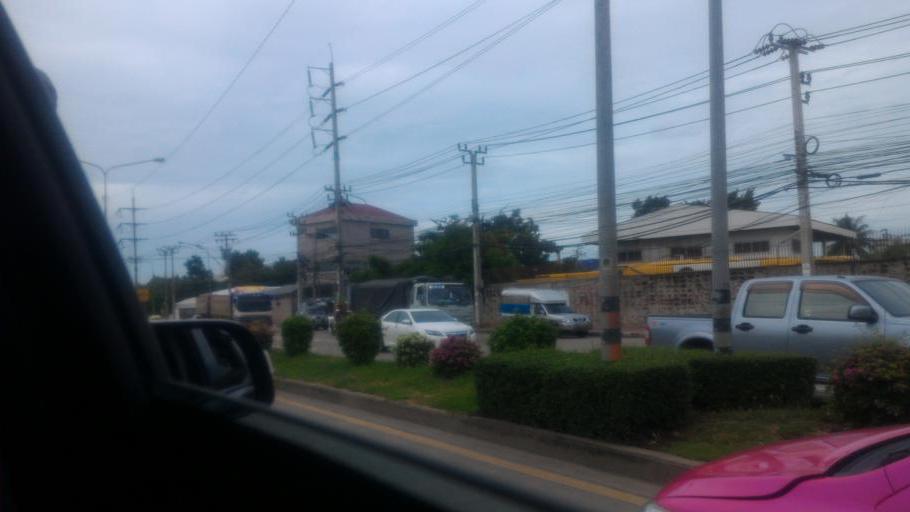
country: TH
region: Bangkok
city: Bang Khun Thian
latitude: 13.6259
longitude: 100.4349
